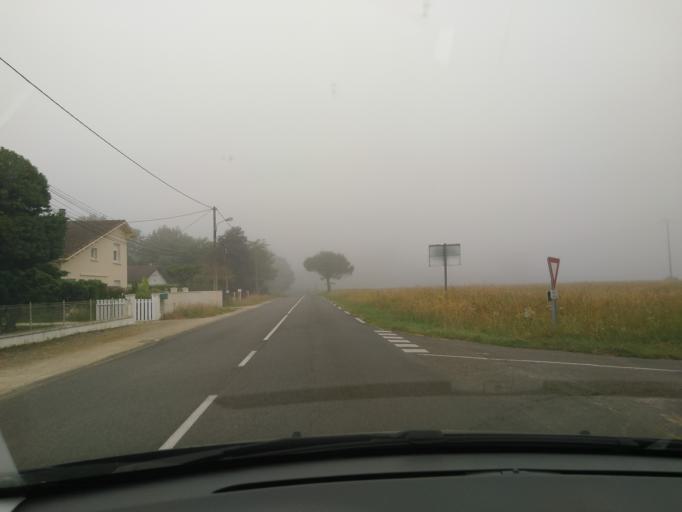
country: FR
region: Aquitaine
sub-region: Departement des Landes
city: Villeneuve-de-Marsan
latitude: 43.8905
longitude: -0.3170
